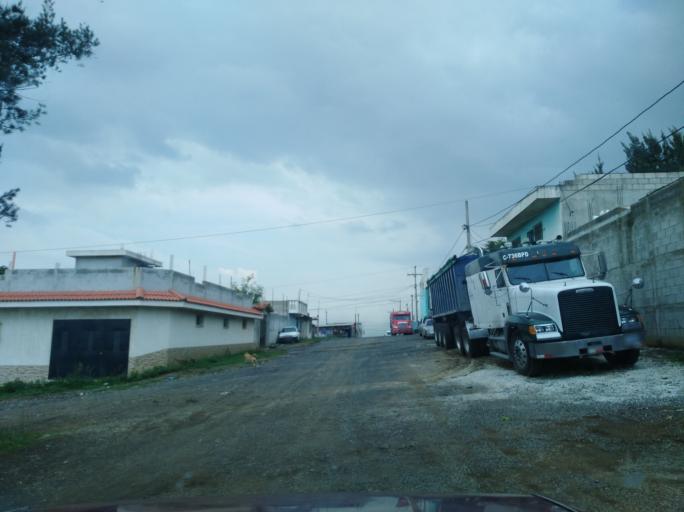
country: GT
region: Guatemala
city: Villa Nueva
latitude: 14.5246
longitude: -90.6219
